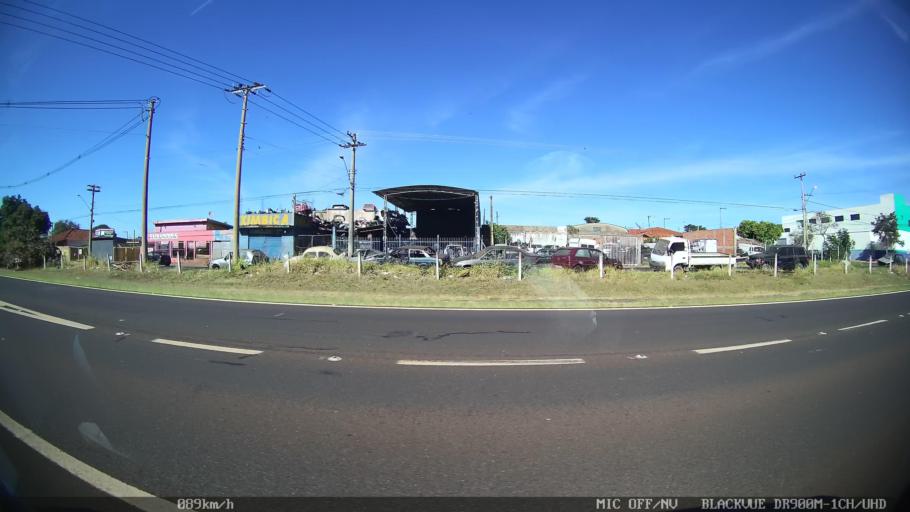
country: BR
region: Sao Paulo
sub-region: Franca
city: Franca
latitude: -20.5731
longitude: -47.3765
